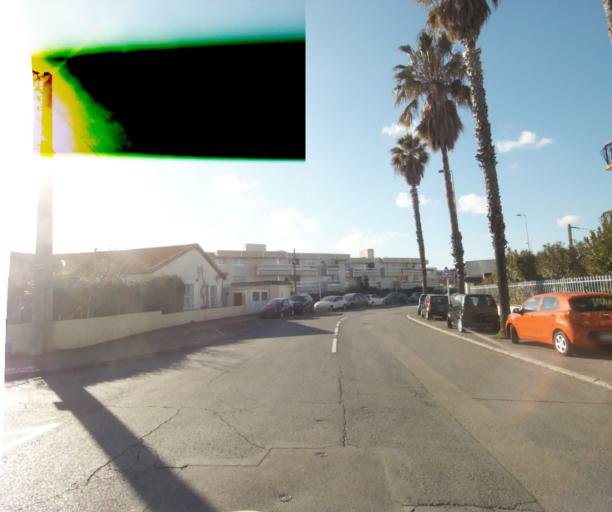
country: FR
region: Provence-Alpes-Cote d'Azur
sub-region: Departement des Alpes-Maritimes
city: Antibes
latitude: 43.5996
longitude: 7.1243
